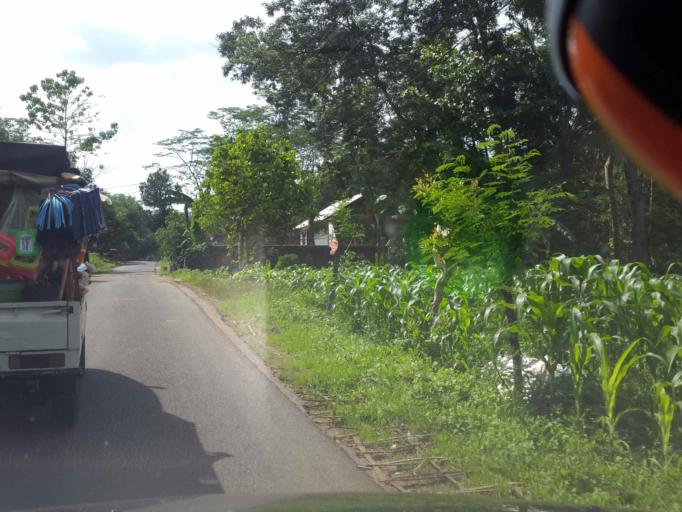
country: ID
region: Central Java
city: Gombong
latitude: -7.4568
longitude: 109.6001
